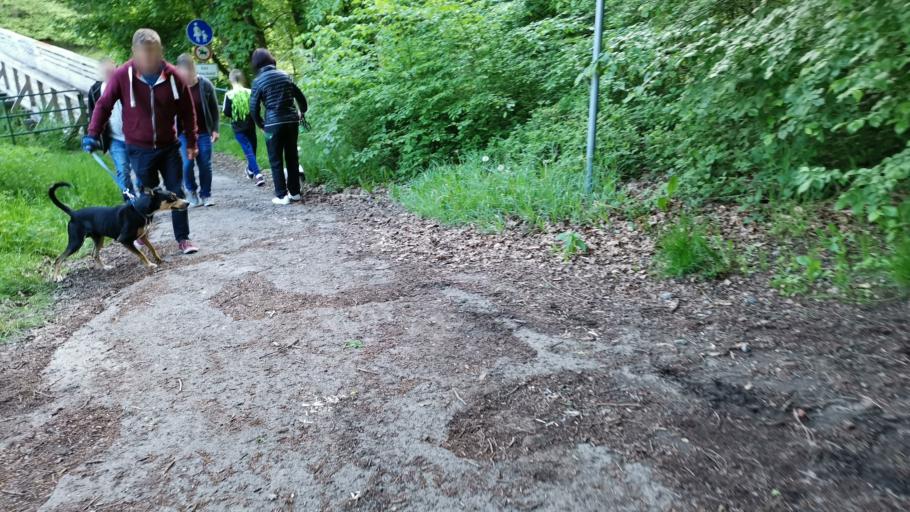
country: DE
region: Saarland
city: Kirkel
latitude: 49.2484
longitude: 7.1873
